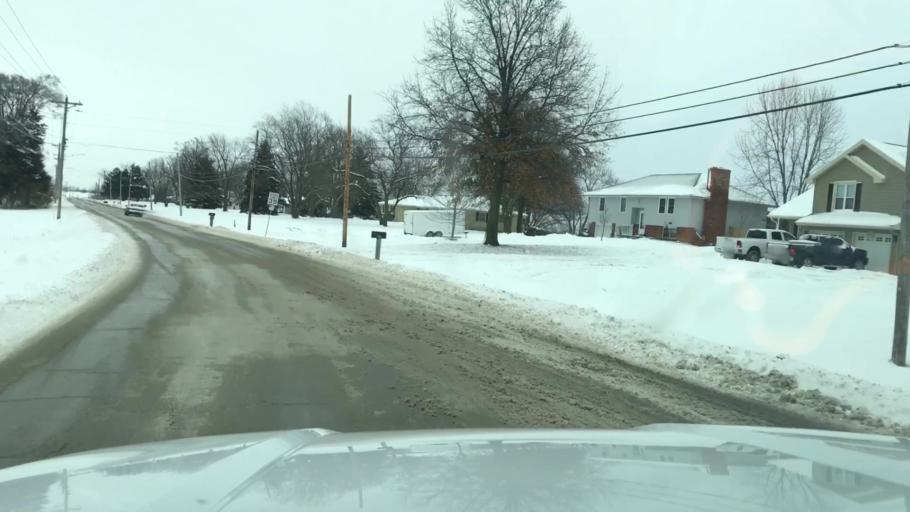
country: US
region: Missouri
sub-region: Clinton County
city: Cameron
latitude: 39.7424
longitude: -94.2252
